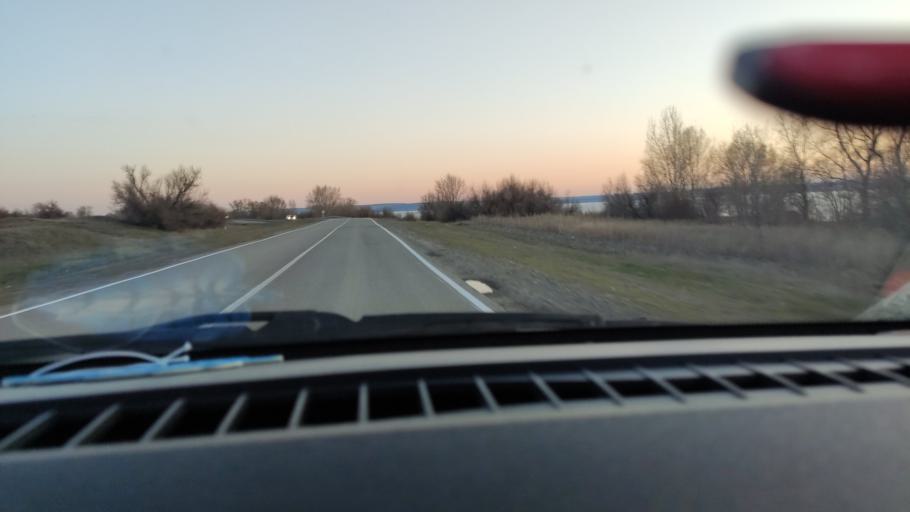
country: RU
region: Saratov
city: Privolzhskiy
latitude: 51.2153
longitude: 45.9186
